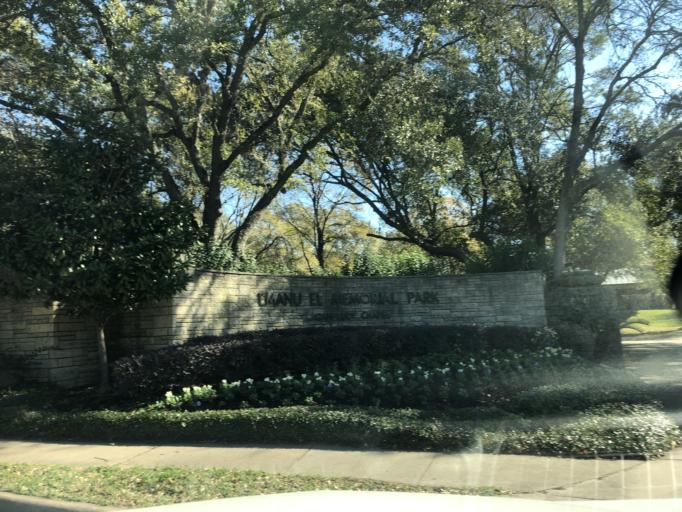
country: US
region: Texas
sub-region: Fort Bend County
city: Missouri City
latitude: 29.6793
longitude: -95.5235
